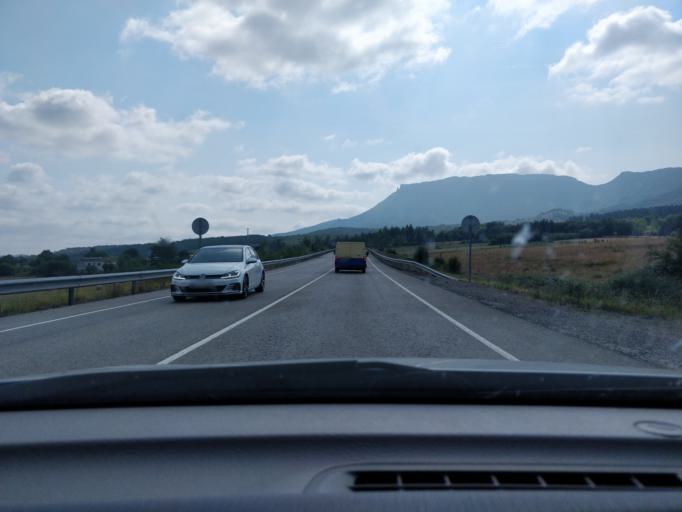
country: ES
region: Castille and Leon
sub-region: Provincia de Burgos
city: Villasana de Mena
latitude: 43.0938
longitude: -3.2871
